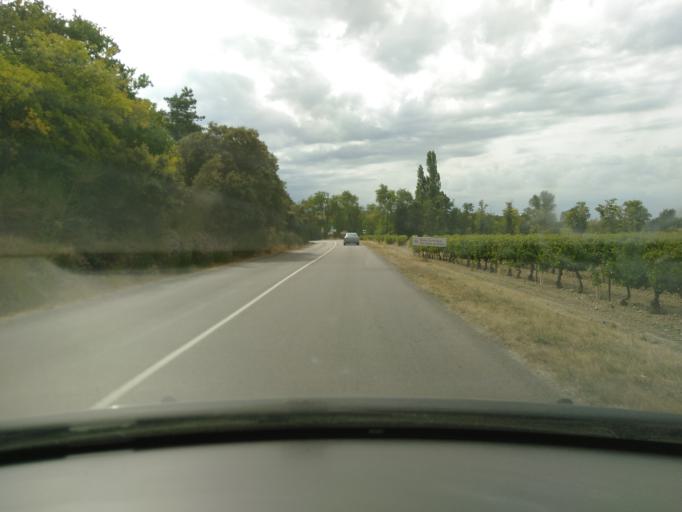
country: FR
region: Rhone-Alpes
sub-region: Departement de la Drome
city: Taulignan
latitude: 44.4395
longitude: 5.0184
